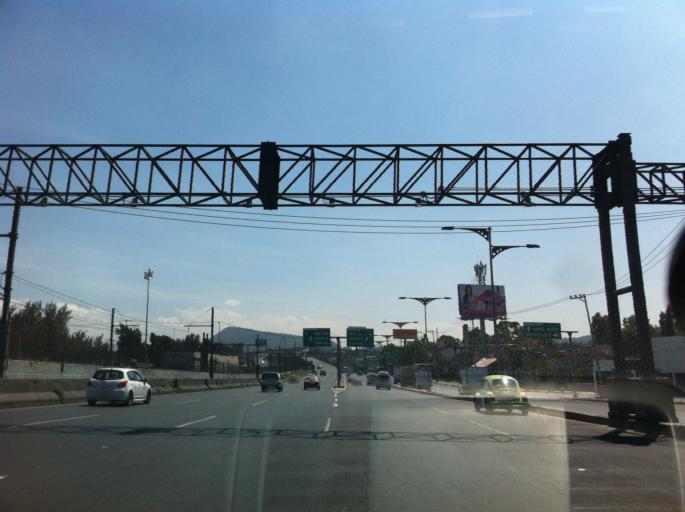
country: MX
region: Mexico
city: Los Reyes La Paz
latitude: 19.3644
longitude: -99.0056
